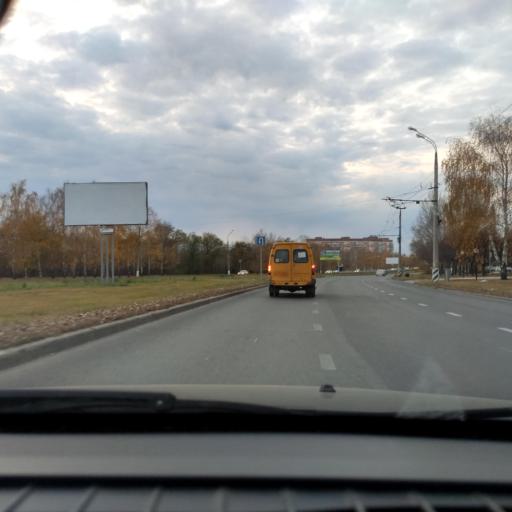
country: RU
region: Samara
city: Tol'yatti
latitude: 53.5003
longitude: 49.2679
